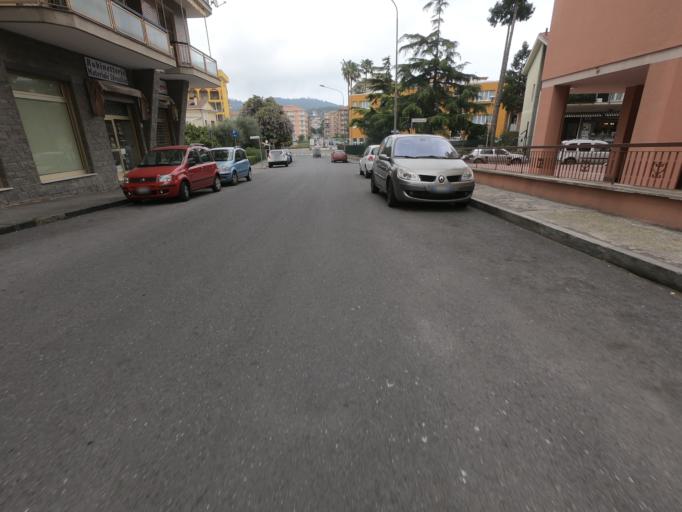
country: IT
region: Liguria
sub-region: Provincia di Savona
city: Andora
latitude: 43.9524
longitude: 8.1401
